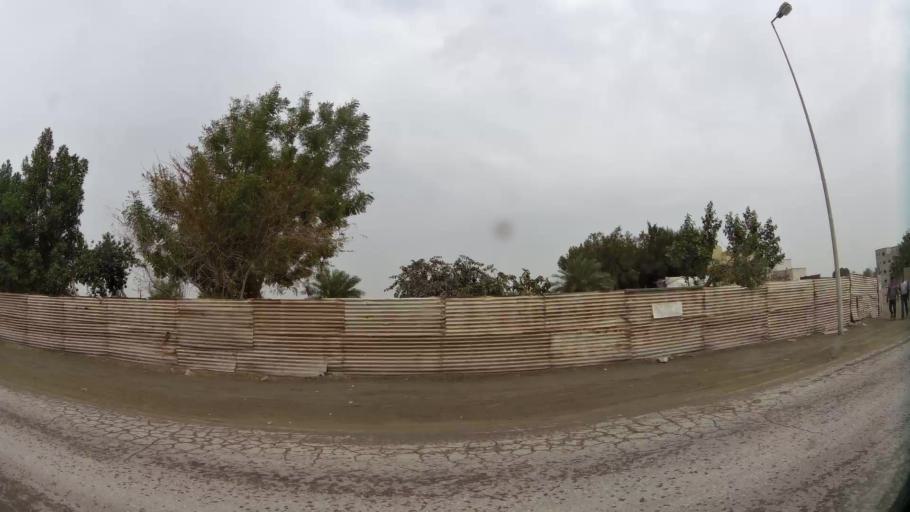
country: BH
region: Northern
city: Ar Rifa'
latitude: 26.1342
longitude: 50.5896
